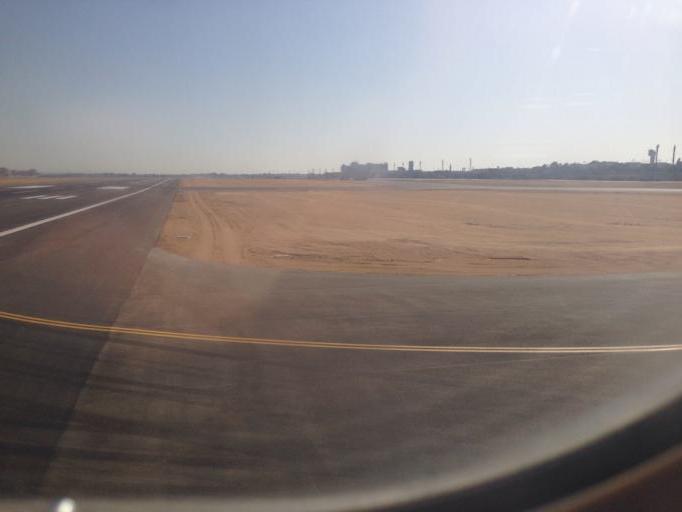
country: EG
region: Muhafazat al Qalyubiyah
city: Al Khankah
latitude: 30.1204
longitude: 31.3817
